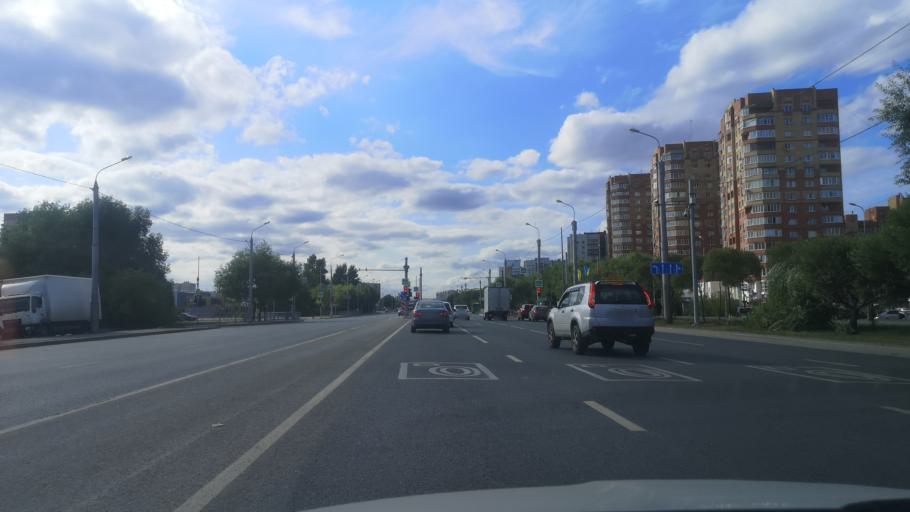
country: RU
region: Tjumen
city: Tyumen
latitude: 57.1169
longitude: 65.5628
